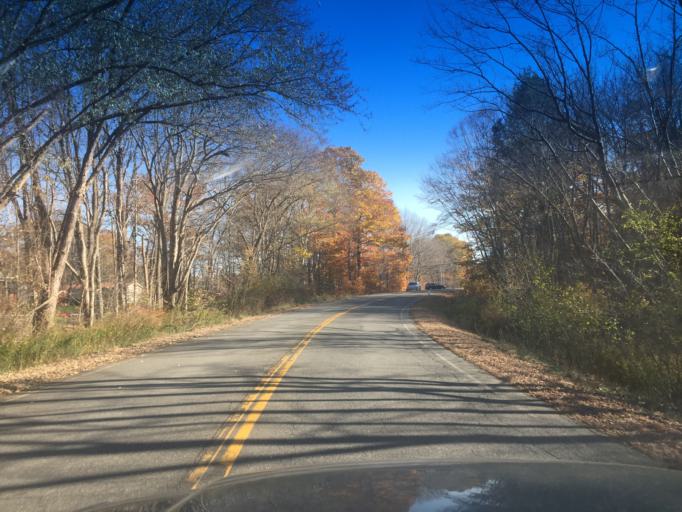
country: US
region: Maine
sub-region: York County
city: Kittery Point
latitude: 43.1278
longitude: -70.7125
